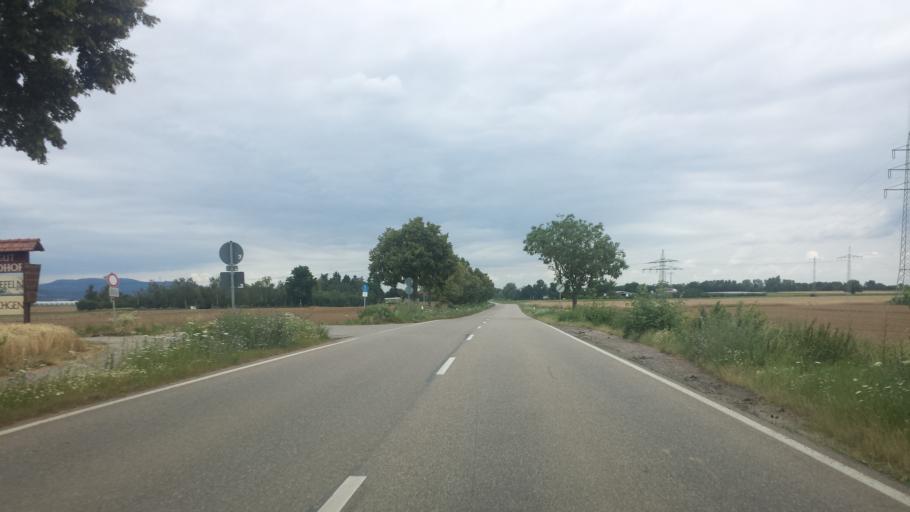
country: DE
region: Rheinland-Pfalz
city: Meckenheim
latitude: 49.3861
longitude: 8.2478
